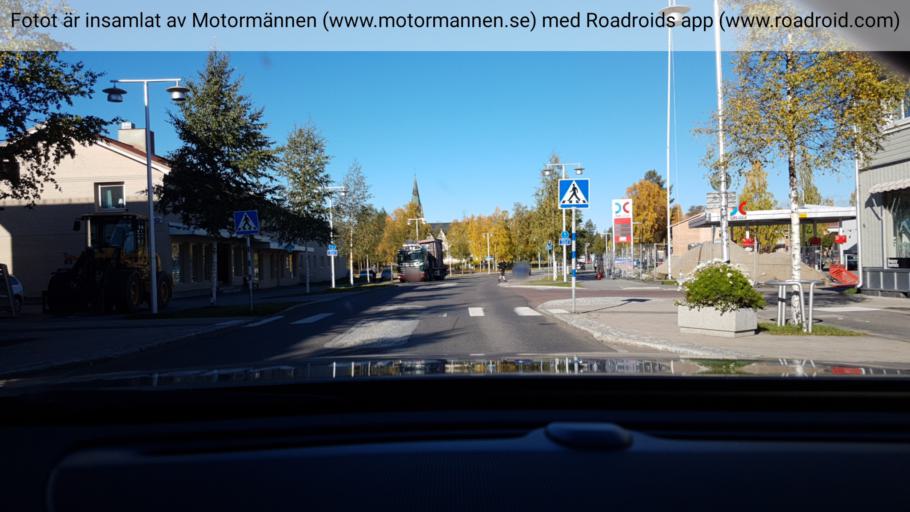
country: SE
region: Norrbotten
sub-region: Arvidsjaurs Kommun
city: Arvidsjaur
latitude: 65.5942
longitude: 19.1713
